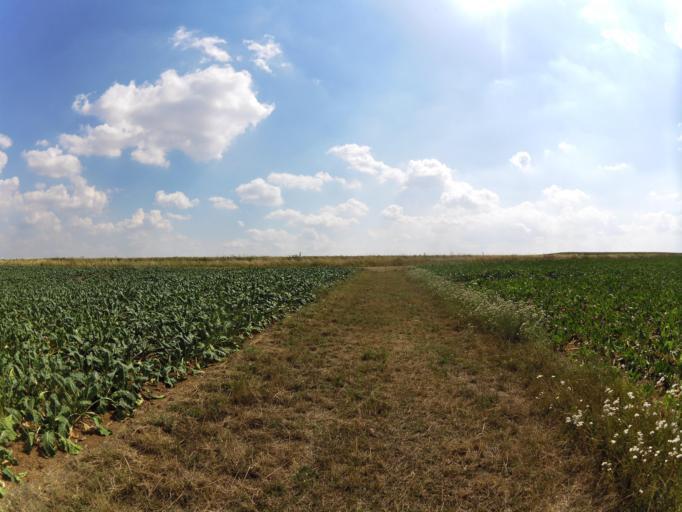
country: DE
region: Bavaria
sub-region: Regierungsbezirk Unterfranken
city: Ochsenfurt
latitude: 49.6381
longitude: 10.0592
